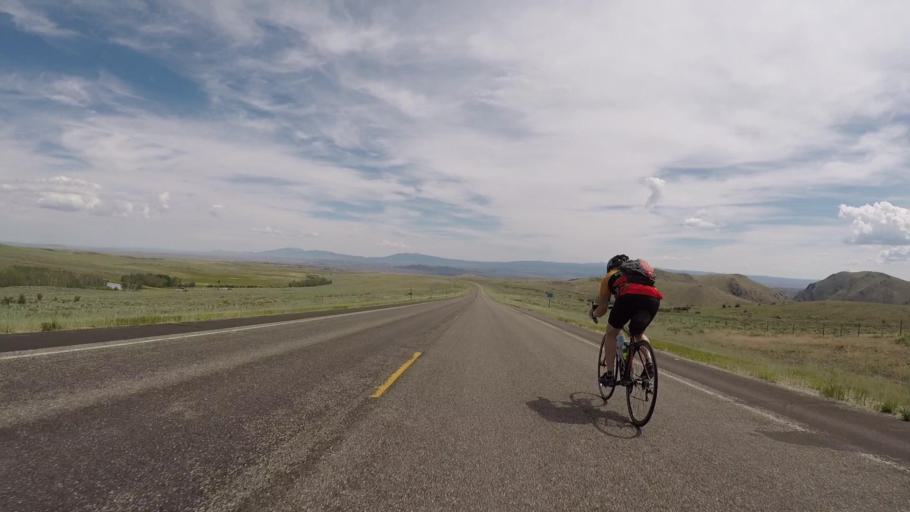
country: US
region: Wyoming
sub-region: Carbon County
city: Saratoga
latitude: 41.1845
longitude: -106.8615
